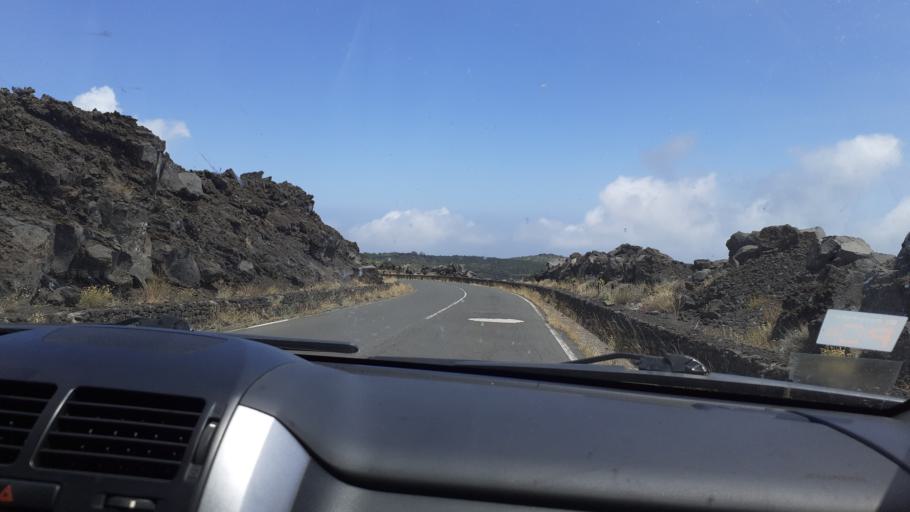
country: IT
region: Sicily
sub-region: Catania
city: Nicolosi
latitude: 37.6859
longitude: 15.0206
